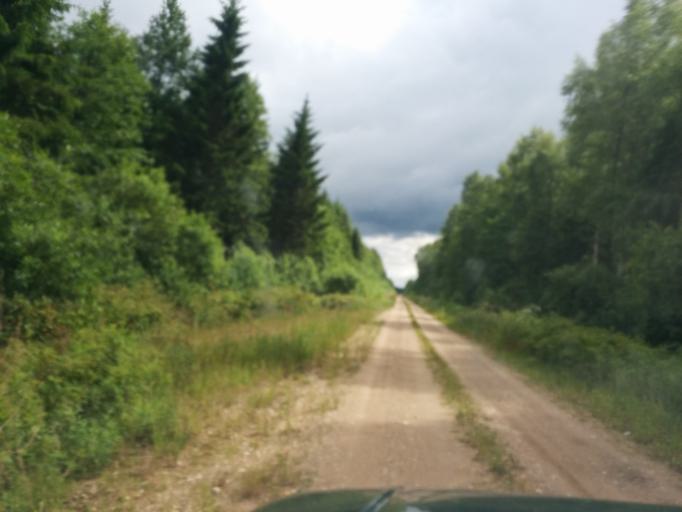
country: LV
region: Vilaka
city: Vilaka
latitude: 57.3935
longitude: 27.6351
